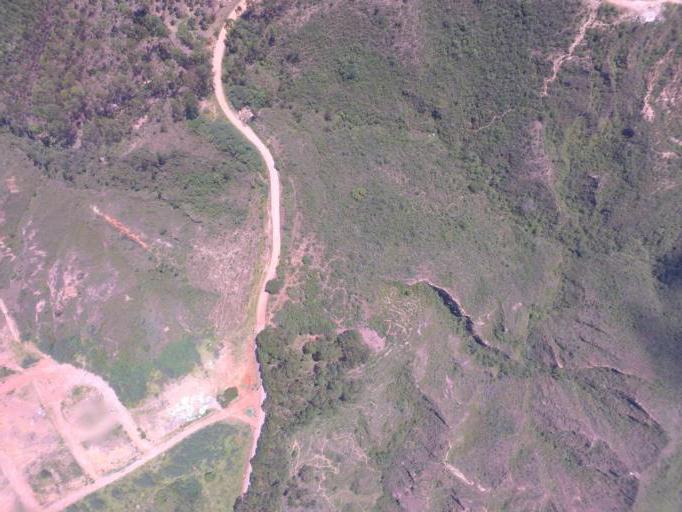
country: BR
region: Minas Gerais
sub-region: Tiradentes
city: Tiradentes
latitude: -21.0515
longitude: -44.0831
